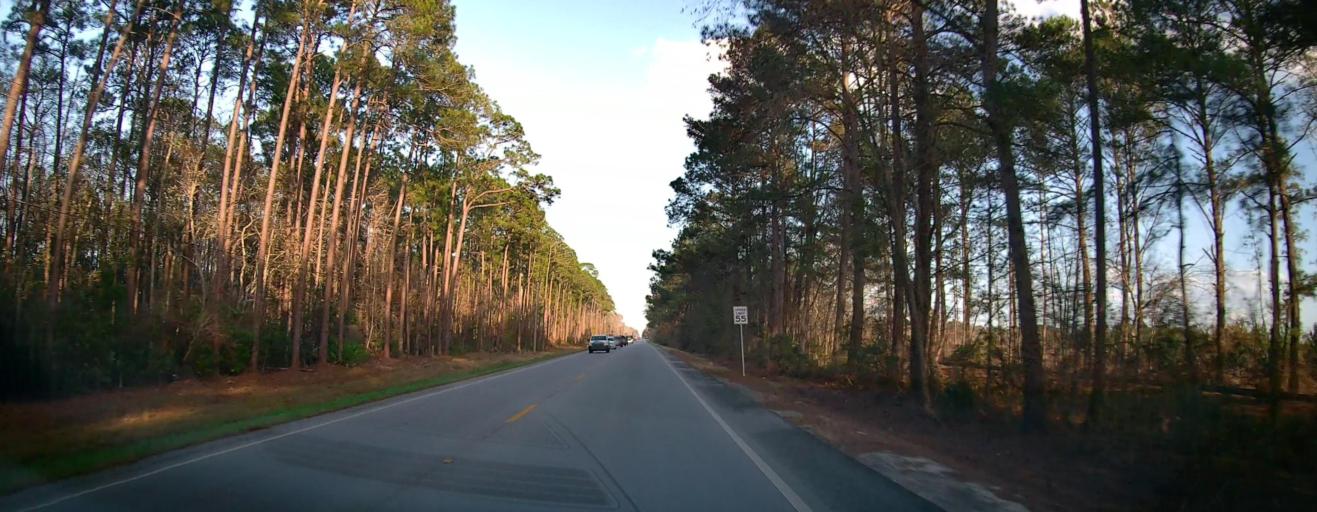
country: US
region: Georgia
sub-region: Bryan County
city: Pembroke
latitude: 32.1409
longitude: -81.6966
